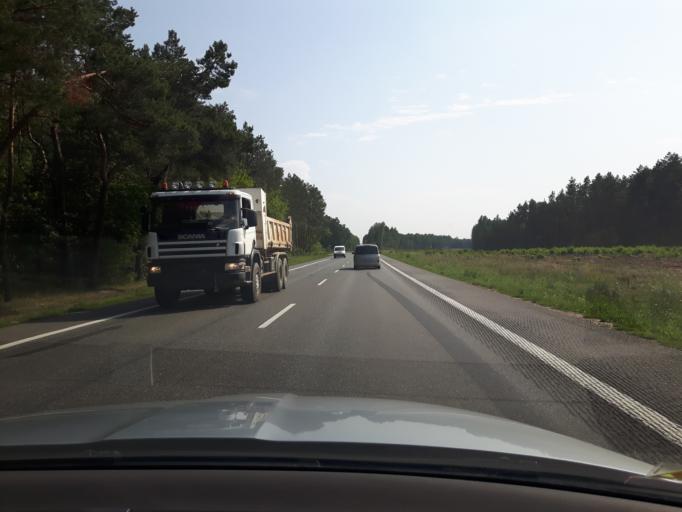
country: PL
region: Masovian Voivodeship
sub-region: Powiat mlawski
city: Strzegowo
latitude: 52.9228
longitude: 20.2861
